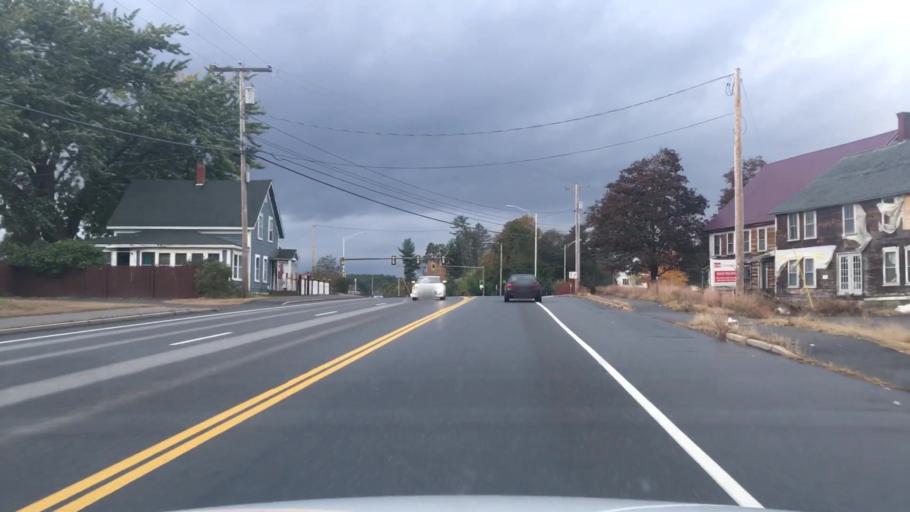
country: US
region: New Hampshire
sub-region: Merrimack County
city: Epsom
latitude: 43.2261
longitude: -71.3491
